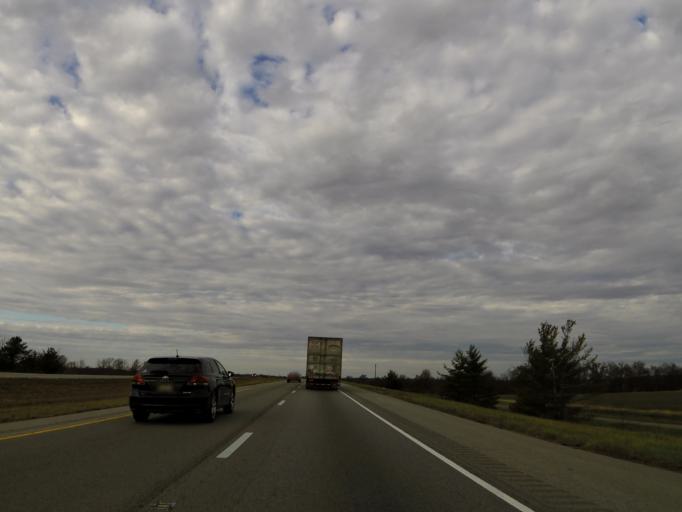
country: US
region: Illinois
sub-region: Clinton County
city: Wamac
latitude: 38.3623
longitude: -89.0677
